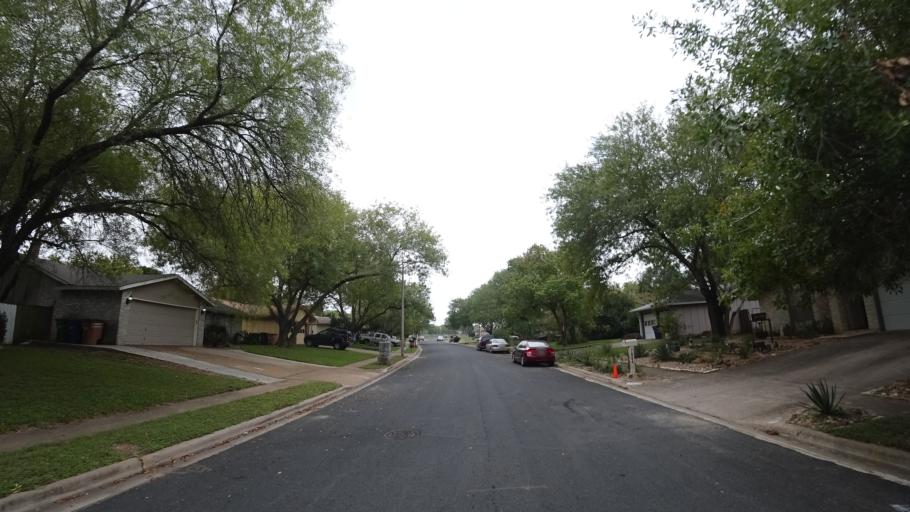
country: US
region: Texas
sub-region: Travis County
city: Shady Hollow
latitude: 30.2054
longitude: -97.8374
